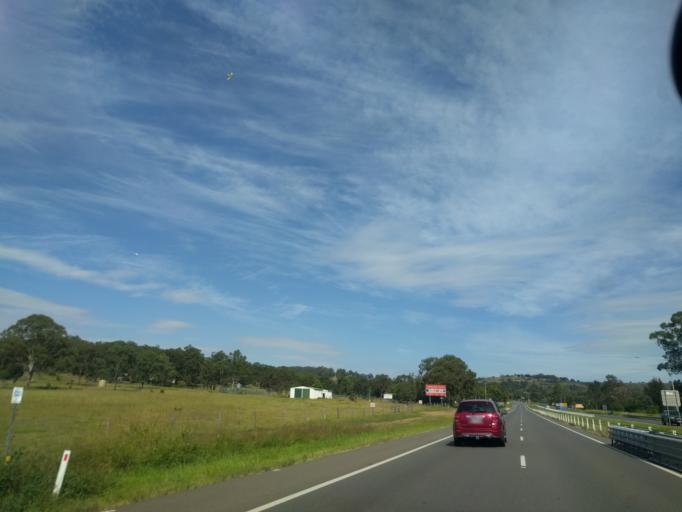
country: AU
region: Queensland
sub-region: Ipswich
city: Thagoona
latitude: -27.5554
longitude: 152.5436
